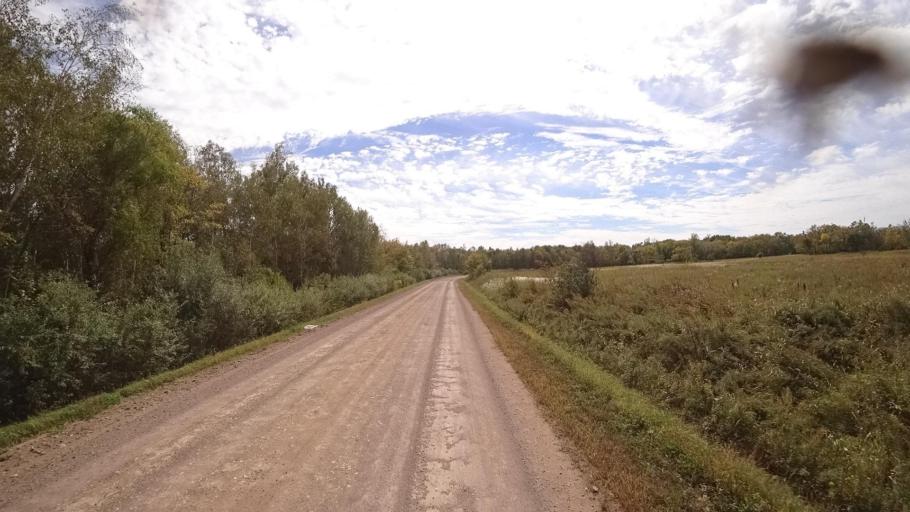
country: RU
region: Primorskiy
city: Yakovlevka
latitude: 44.5357
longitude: 133.6052
